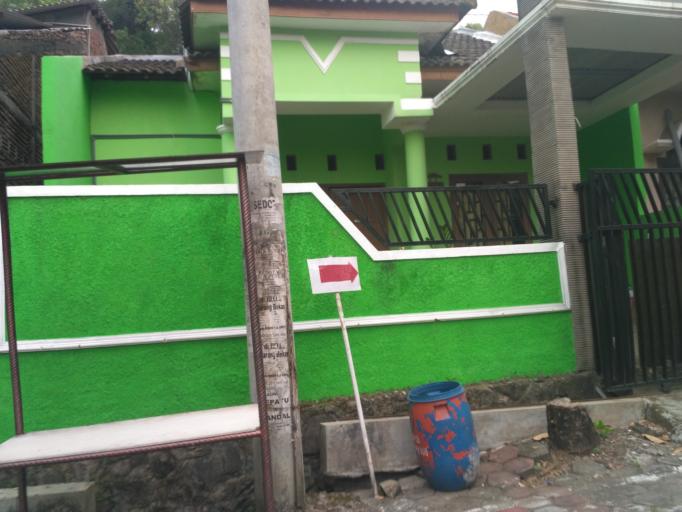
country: ID
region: Central Java
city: Mranggen
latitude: -7.0394
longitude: 110.4726
